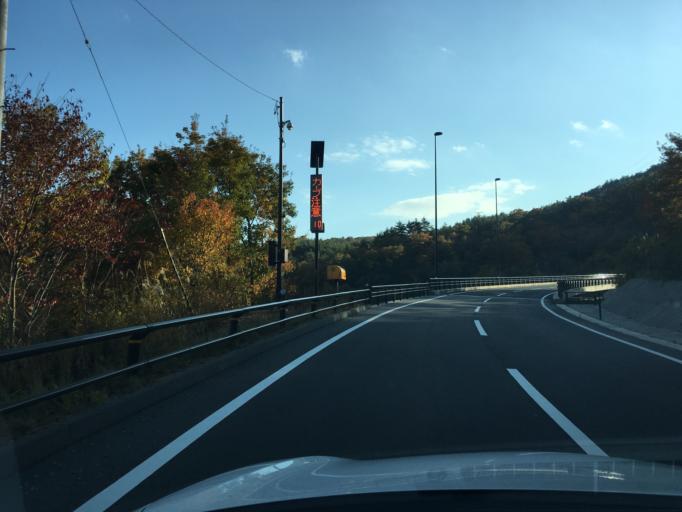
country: JP
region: Fukushima
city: Funehikimachi-funehiki
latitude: 37.2908
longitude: 140.7574
